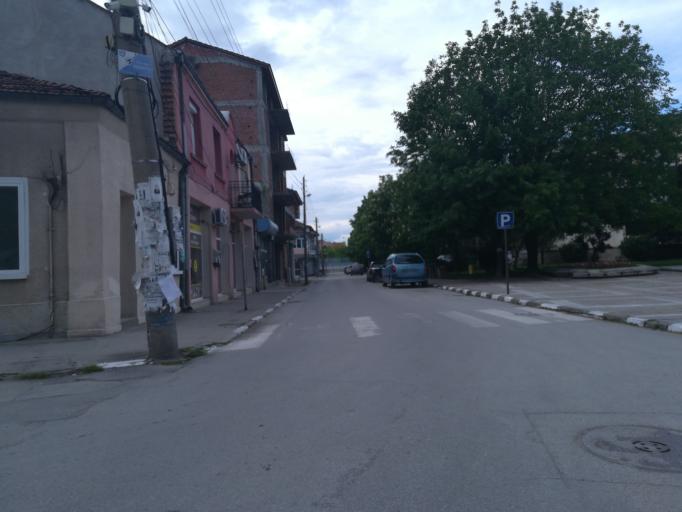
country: BG
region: Stara Zagora
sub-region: Obshtina Chirpan
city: Chirpan
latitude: 42.0987
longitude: 25.2240
